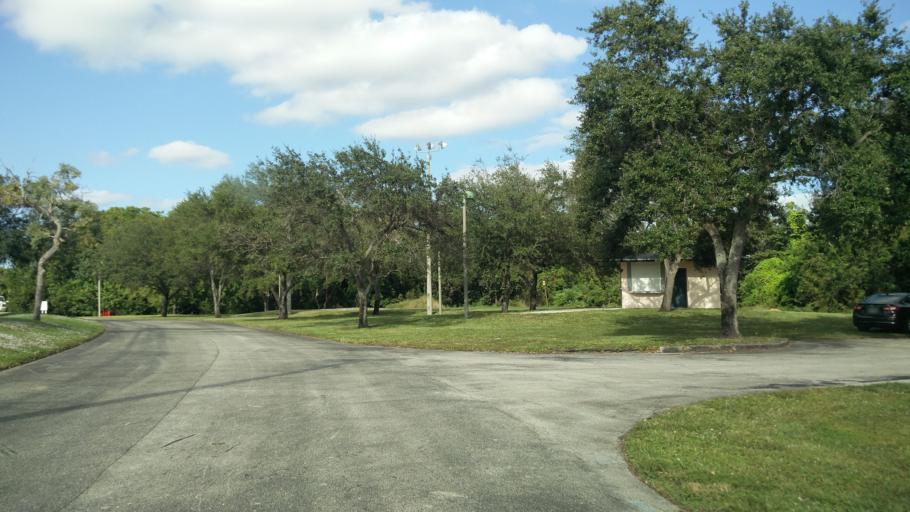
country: US
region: Florida
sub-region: Broward County
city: Rock Island
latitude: 26.1575
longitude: -80.1593
